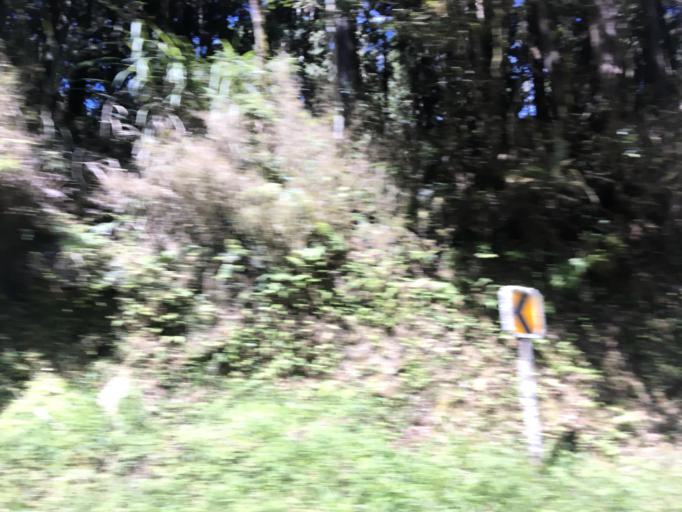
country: TW
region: Taiwan
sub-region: Yilan
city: Yilan
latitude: 24.5205
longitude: 121.5190
